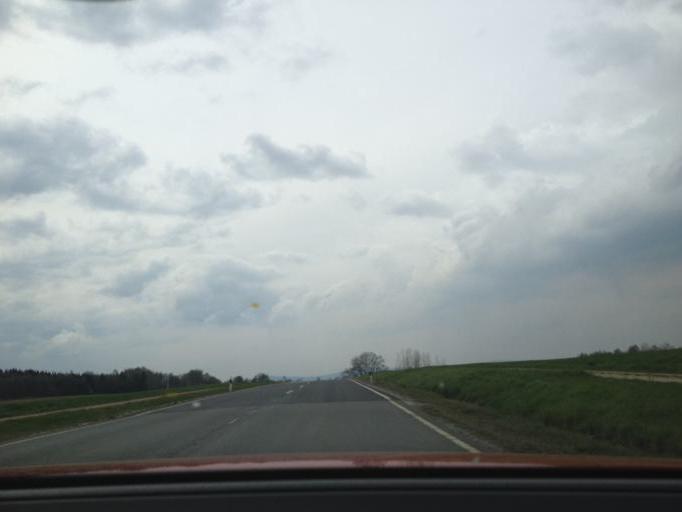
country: DE
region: Bavaria
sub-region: Upper Franconia
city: Bad Alexandersbad
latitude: 50.0226
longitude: 12.0087
